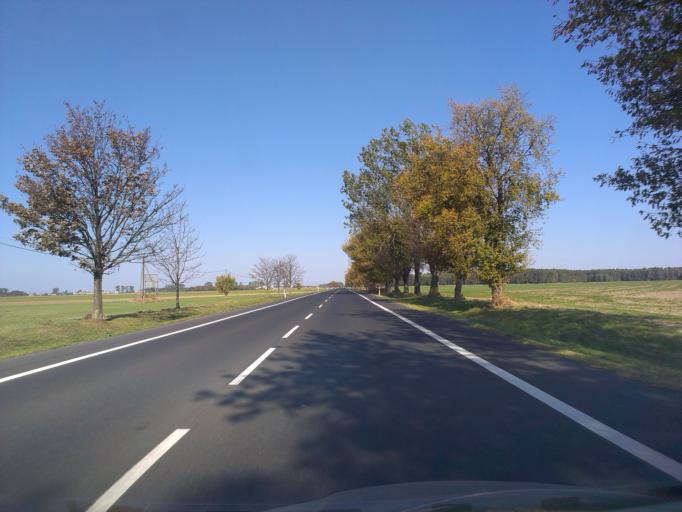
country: PL
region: Greater Poland Voivodeship
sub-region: Powiat obornicki
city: Rogozno
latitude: 52.7855
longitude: 16.9630
